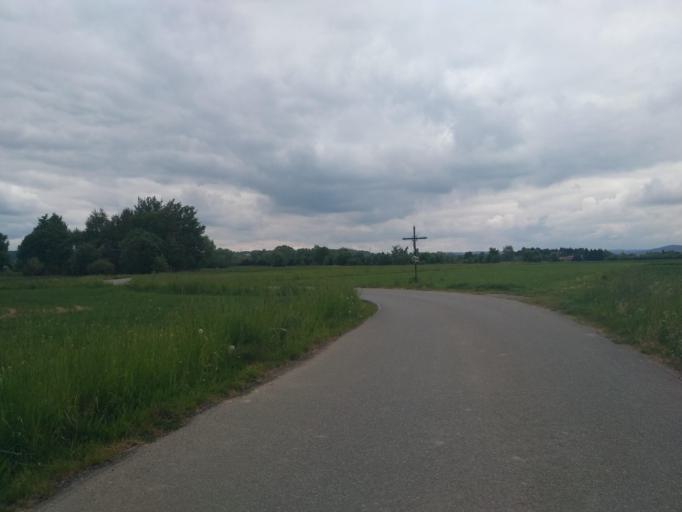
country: PL
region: Subcarpathian Voivodeship
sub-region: Powiat krosnienski
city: Jedlicze
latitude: 49.7045
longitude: 21.6764
